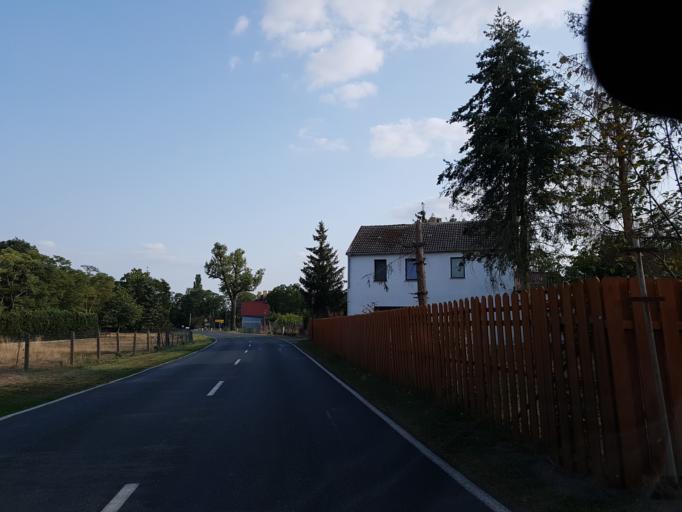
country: DE
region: Saxony
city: Elsnig
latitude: 51.6178
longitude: 12.9084
